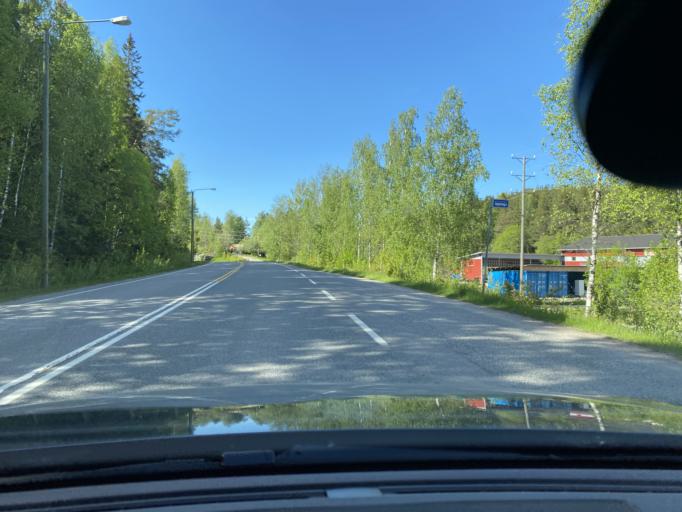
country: FI
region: Varsinais-Suomi
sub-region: Turku
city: Sauvo
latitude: 60.3474
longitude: 22.6822
